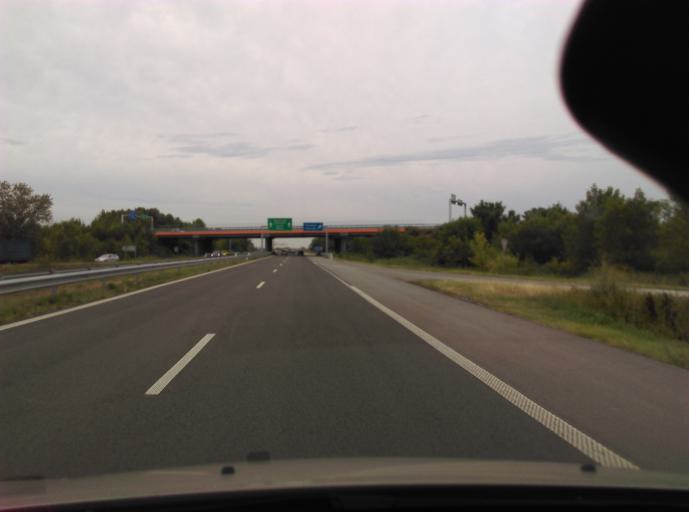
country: BG
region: Plovdiv
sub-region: Obshtina Plovdiv
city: Plovdiv
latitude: 42.2119
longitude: 24.8099
